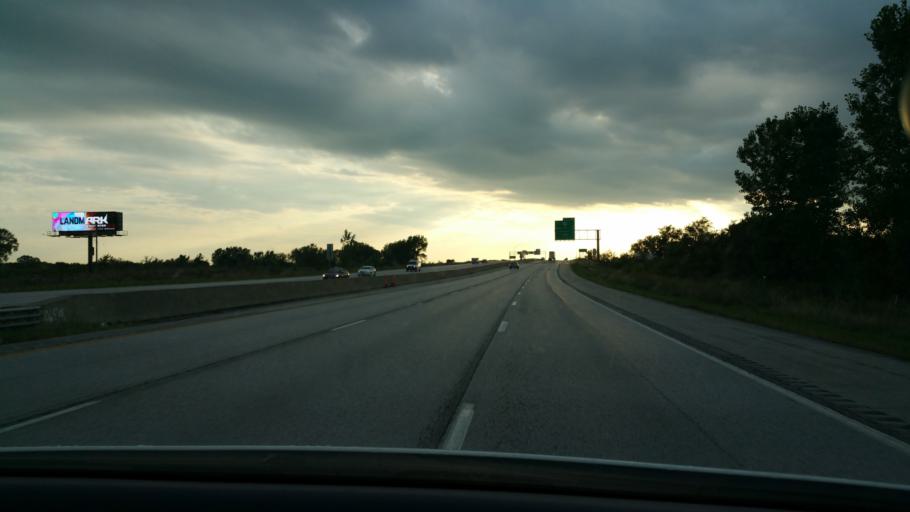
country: US
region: Iowa
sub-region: Polk County
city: Saylorville
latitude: 41.6510
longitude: -93.5847
